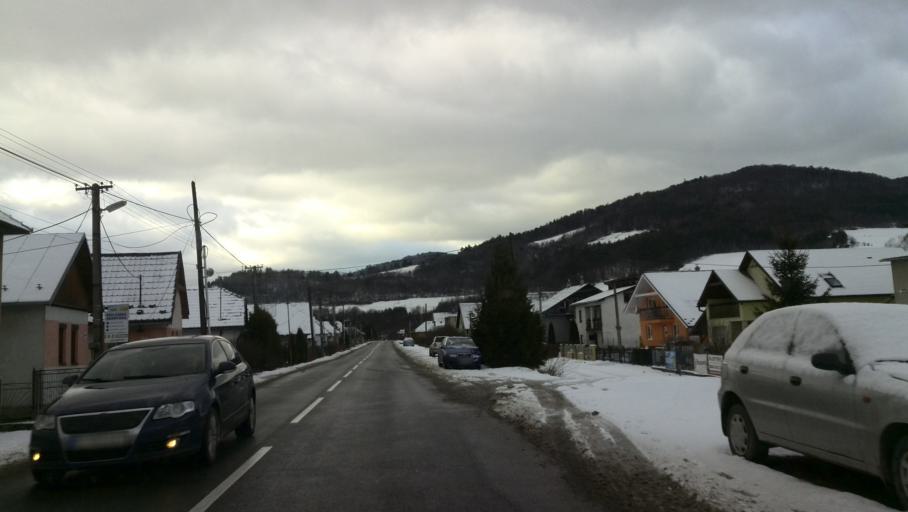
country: SK
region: Kosicky
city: Gelnica
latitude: 48.8736
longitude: 20.9886
